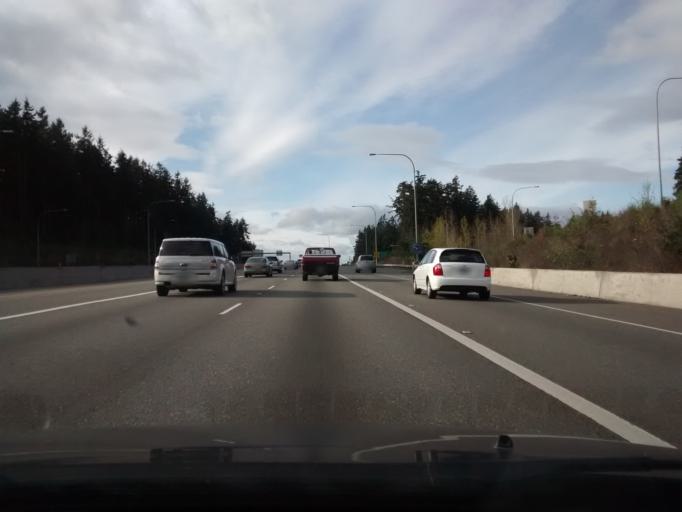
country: US
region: Washington
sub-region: Pierce County
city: Fircrest
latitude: 47.2432
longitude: -122.5047
